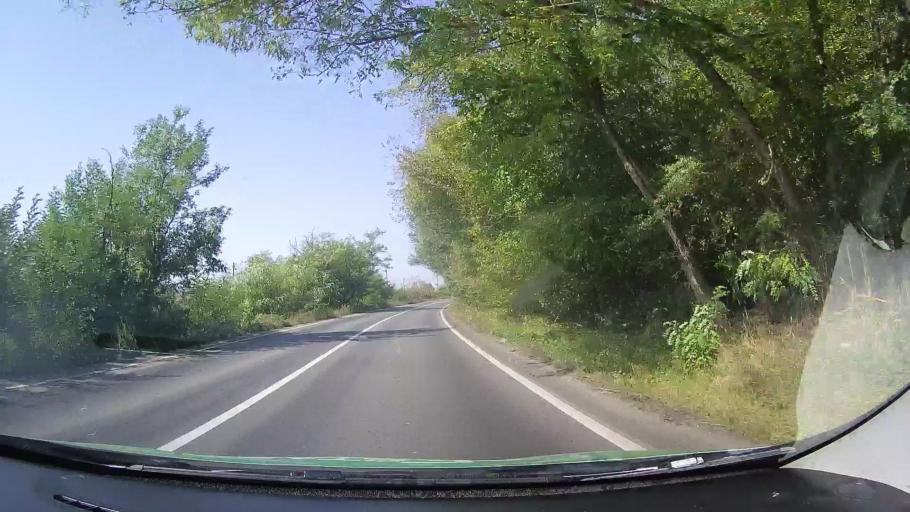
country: RO
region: Arad
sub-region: Comuna Savarsin
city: Savarsin
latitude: 45.9961
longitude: 22.2944
